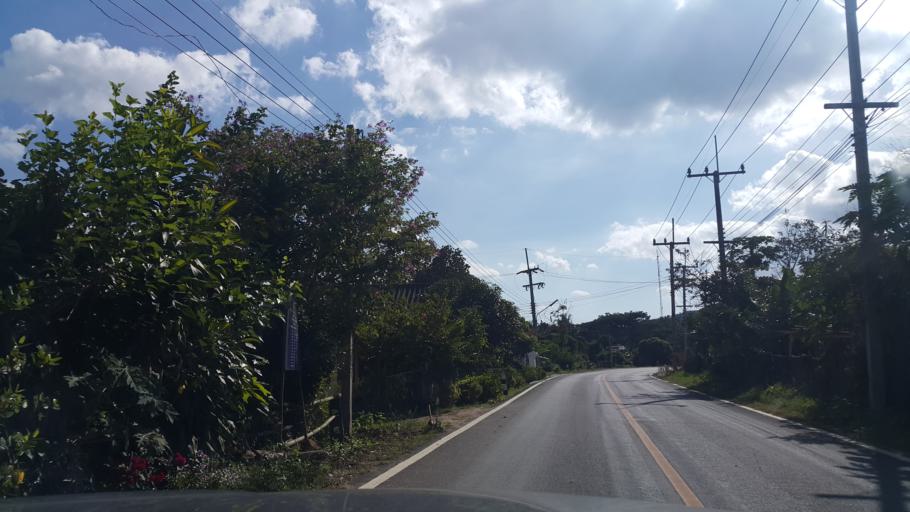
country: TH
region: Lamphun
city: Ban Thi
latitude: 18.5886
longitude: 99.2655
